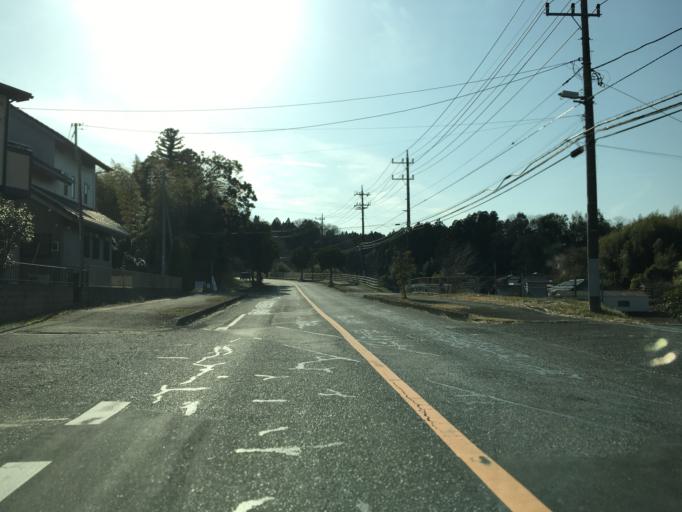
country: JP
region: Ibaraki
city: Takahagi
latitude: 36.7603
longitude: 140.7116
